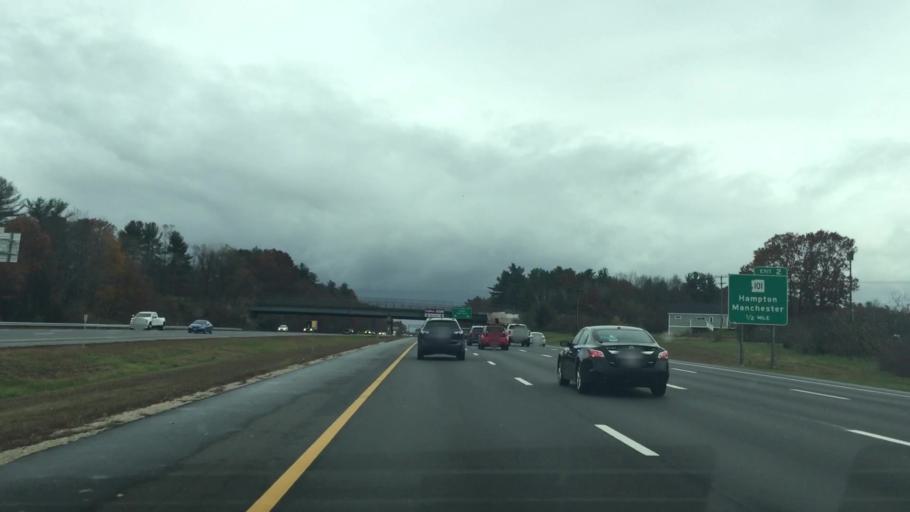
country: US
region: New Hampshire
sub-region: Rockingham County
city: Hampton
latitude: 42.9400
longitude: -70.8608
